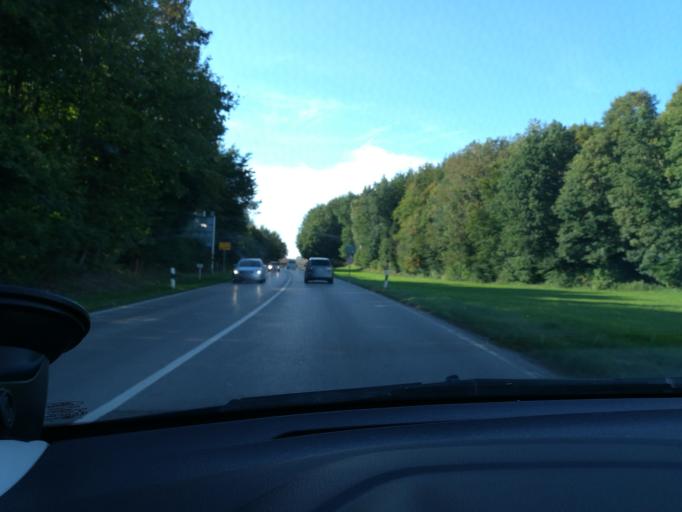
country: DE
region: Bavaria
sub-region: Upper Bavaria
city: Miesbach
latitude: 47.7961
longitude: 11.8395
